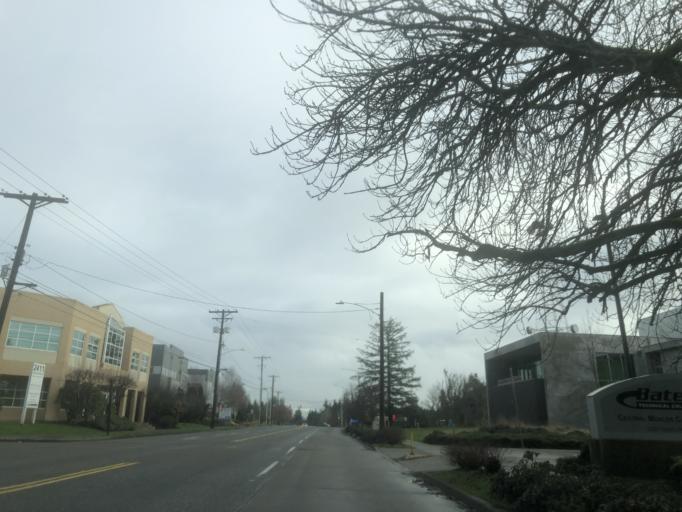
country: US
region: Washington
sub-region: Pierce County
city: Tacoma
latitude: 47.2426
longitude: -122.4692
